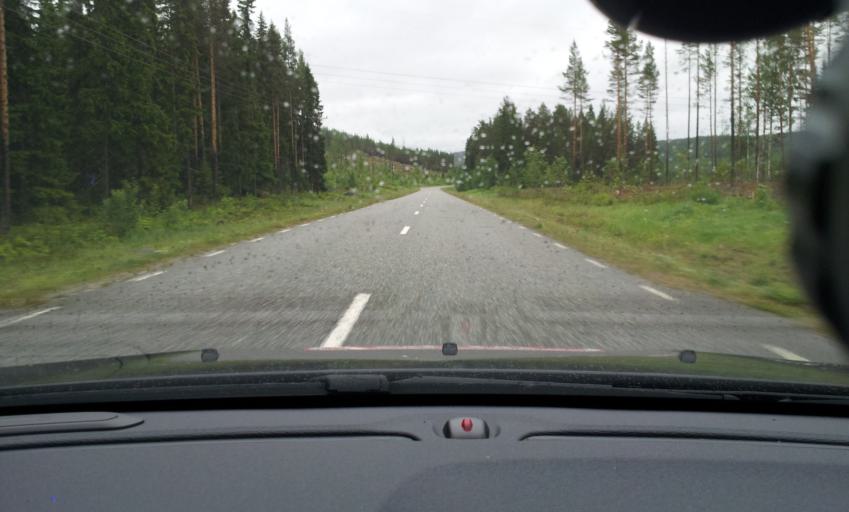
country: SE
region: Jaemtland
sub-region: Ragunda Kommun
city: Hammarstrand
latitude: 63.2755
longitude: 15.8126
